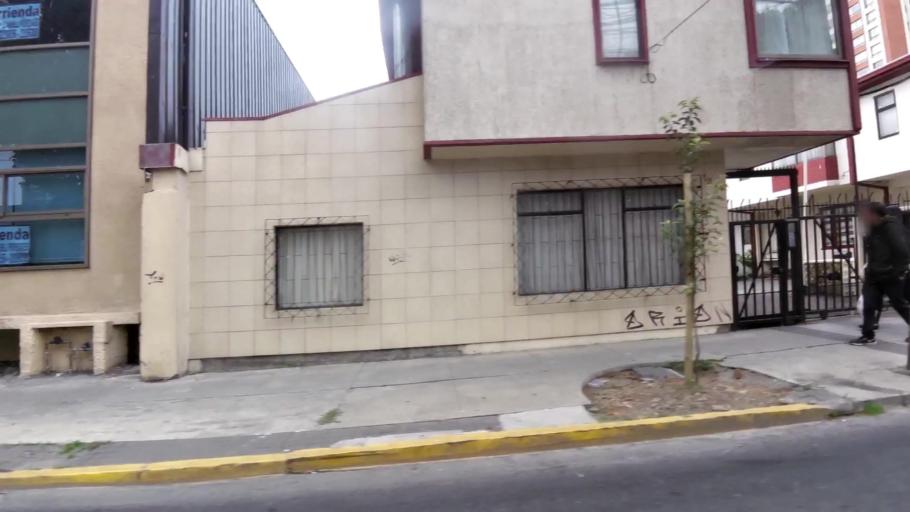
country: CL
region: Biobio
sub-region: Provincia de Concepcion
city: Concepcion
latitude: -36.8225
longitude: -73.0437
